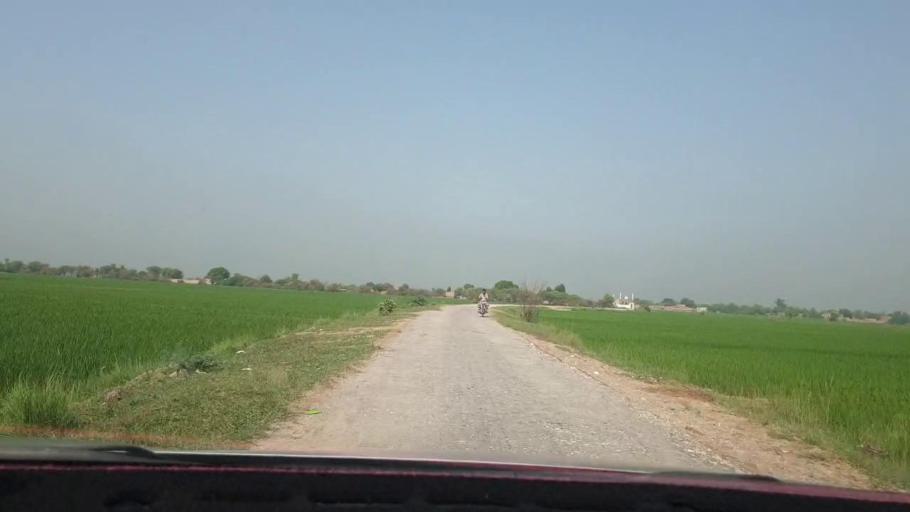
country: PK
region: Sindh
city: Nasirabad
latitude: 27.4313
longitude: 67.8957
